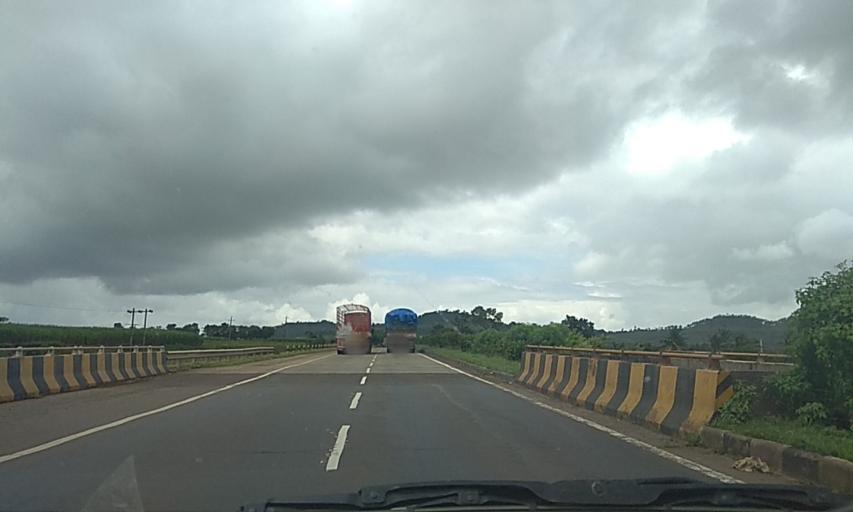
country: IN
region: Karnataka
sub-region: Belgaum
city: Sankeshwar
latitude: 16.2607
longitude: 74.4669
